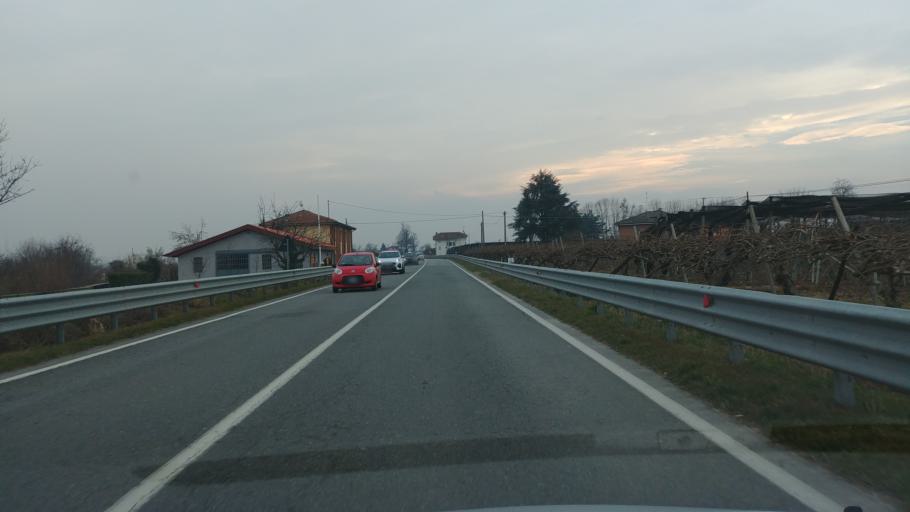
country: IT
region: Piedmont
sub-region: Provincia di Cuneo
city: Sant'Albano Stura
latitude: 44.5046
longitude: 7.6800
